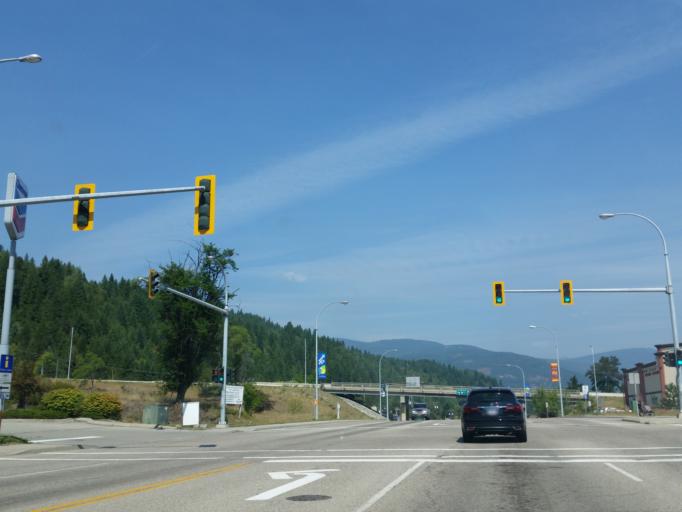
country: CA
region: British Columbia
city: Castlegar
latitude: 49.2972
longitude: -117.6550
